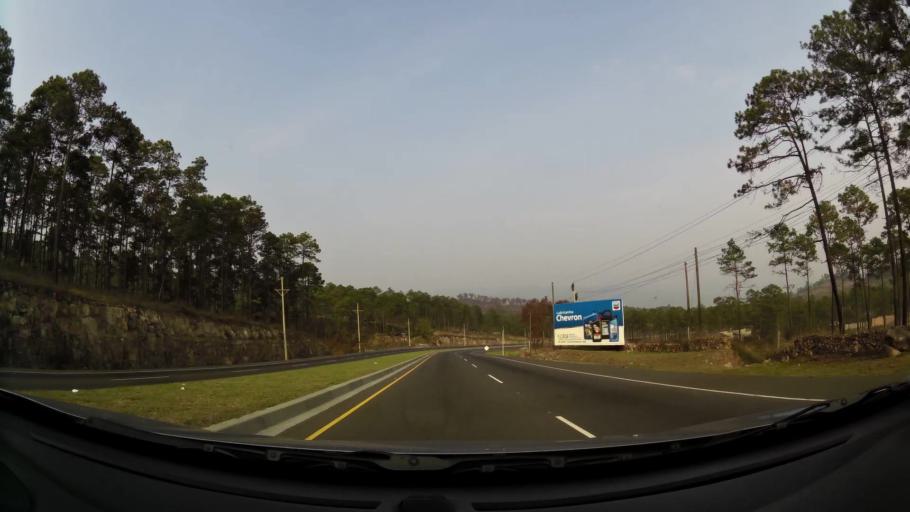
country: HN
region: Francisco Morazan
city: Tamara
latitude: 14.1679
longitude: -87.3095
